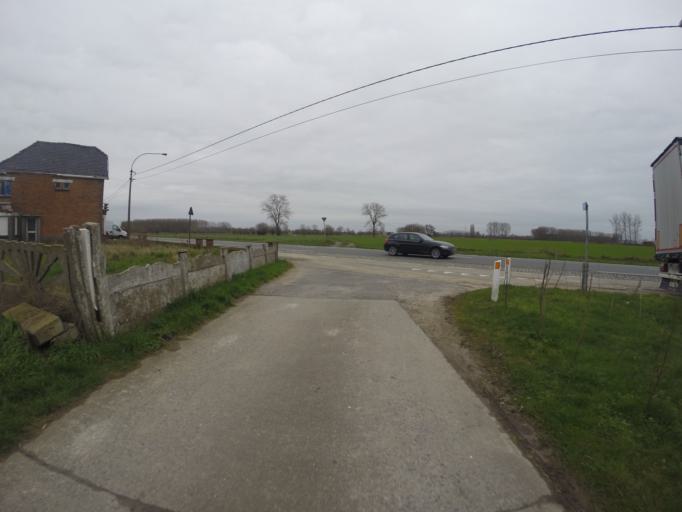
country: BE
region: Flanders
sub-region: Provincie Oost-Vlaanderen
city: Aalter
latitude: 51.1182
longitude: 3.4561
